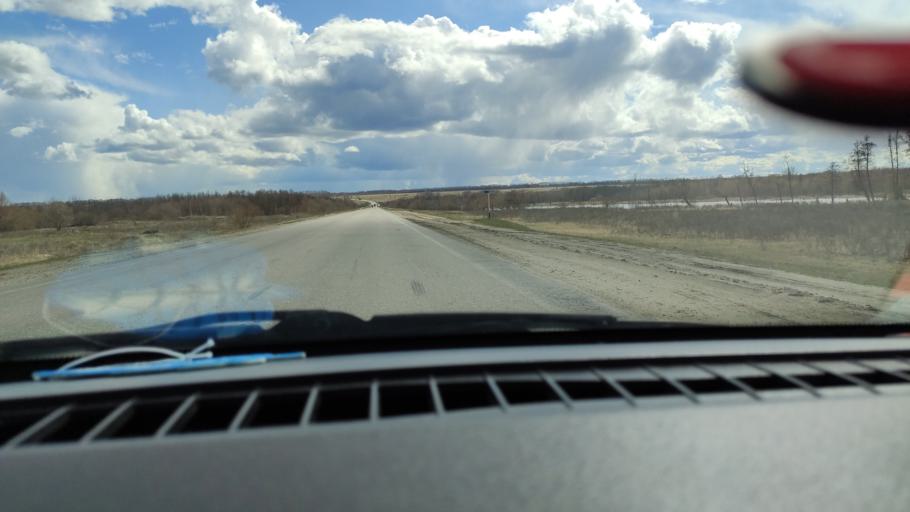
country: RU
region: Samara
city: Varlamovo
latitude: 53.1395
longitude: 48.2856
